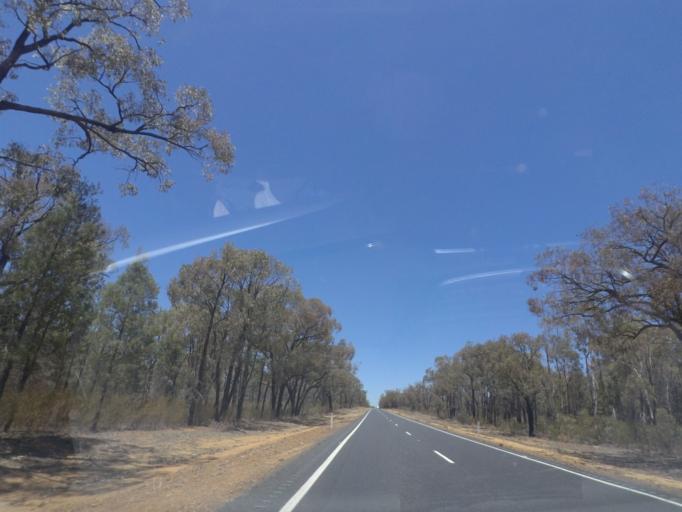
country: AU
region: New South Wales
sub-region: Narrabri
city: Narrabri
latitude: -30.7400
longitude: 149.5160
